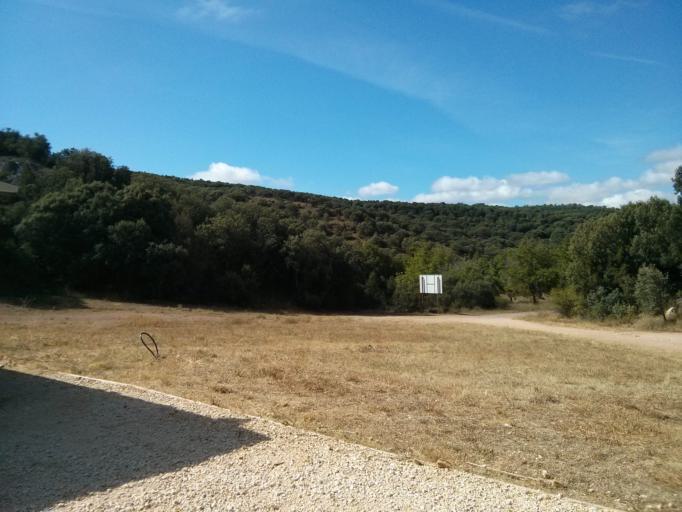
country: ES
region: Castille and Leon
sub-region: Provincia de Burgos
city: Covarrubias
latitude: 42.0602
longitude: -3.4973
